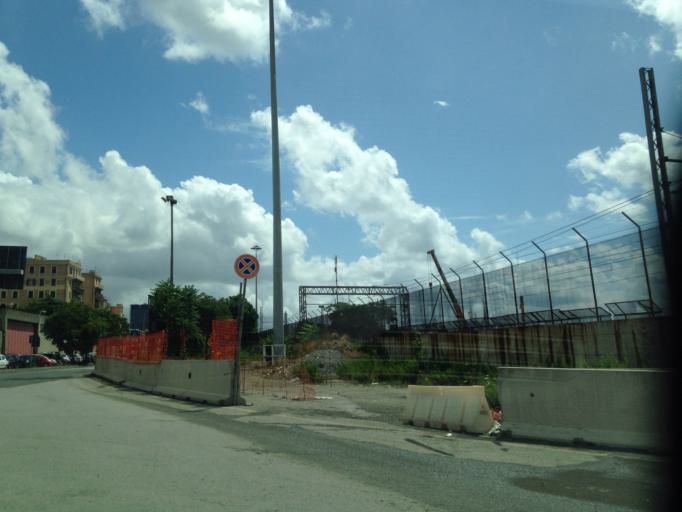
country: IT
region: Liguria
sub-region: Provincia di Genova
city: San Teodoro
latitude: 44.4105
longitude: 8.8840
